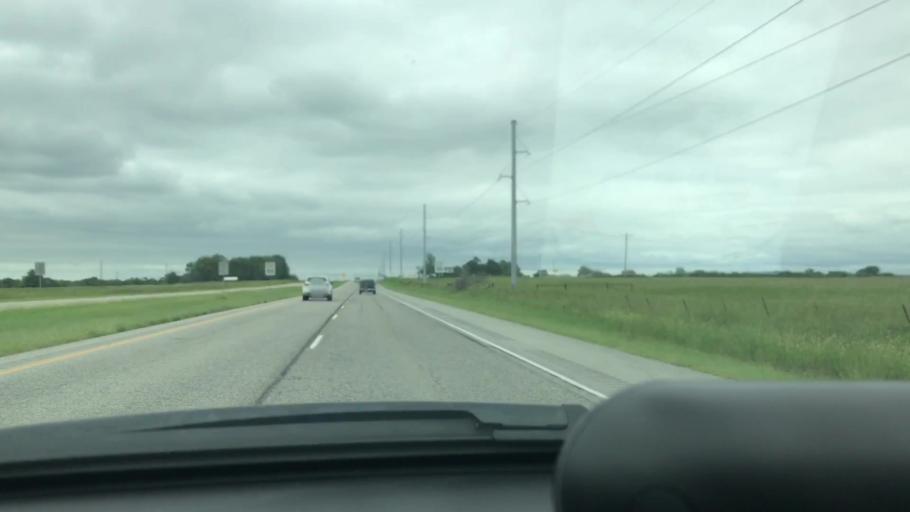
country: US
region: Oklahoma
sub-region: Wagoner County
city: Wagoner
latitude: 36.0109
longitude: -95.3686
